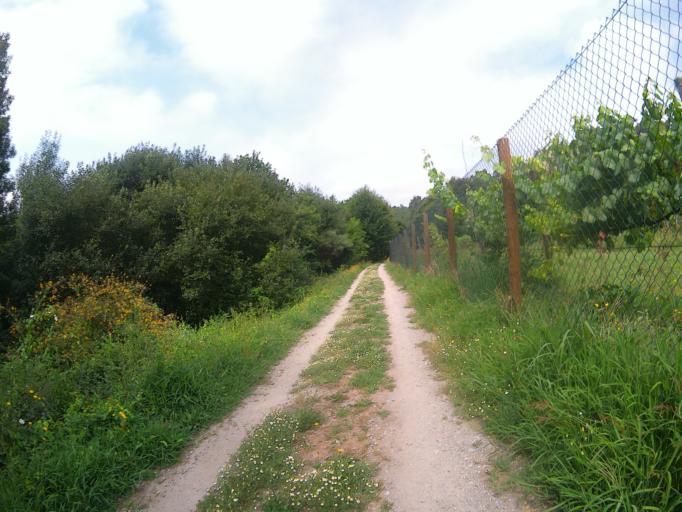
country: PT
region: Viana do Castelo
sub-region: Ponte de Lima
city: Ponte de Lima
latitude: 41.7843
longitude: -8.5303
